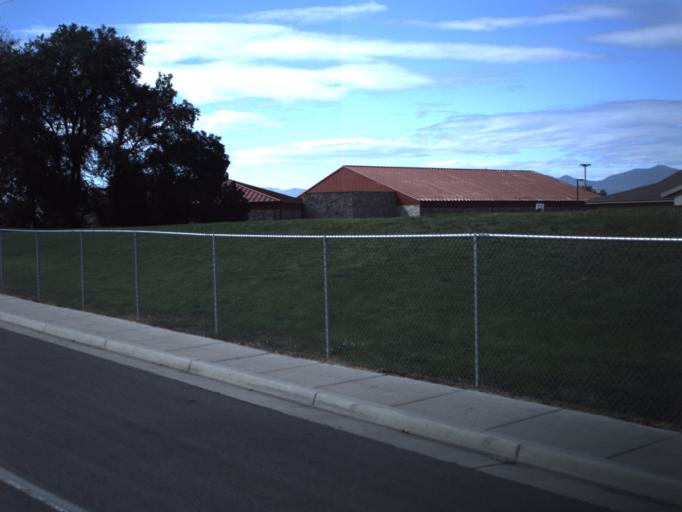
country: US
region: Utah
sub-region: Salt Lake County
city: Salt Lake City
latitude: 40.7932
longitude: -111.9393
